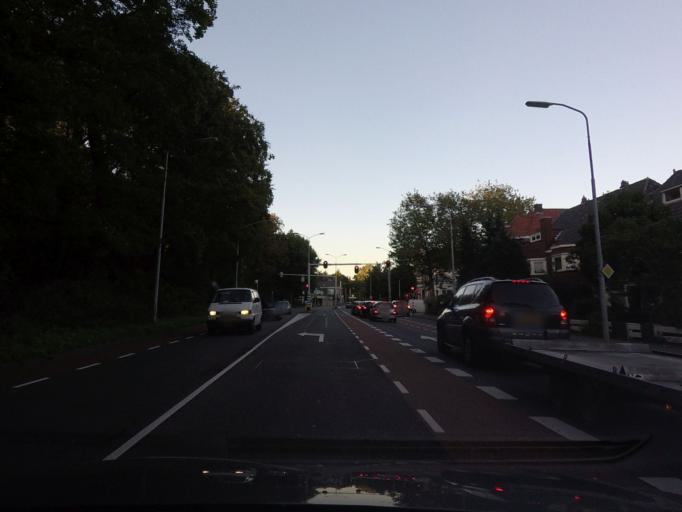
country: NL
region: North Holland
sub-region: Gemeente Alkmaar
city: Alkmaar
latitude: 52.6245
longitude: 4.7372
